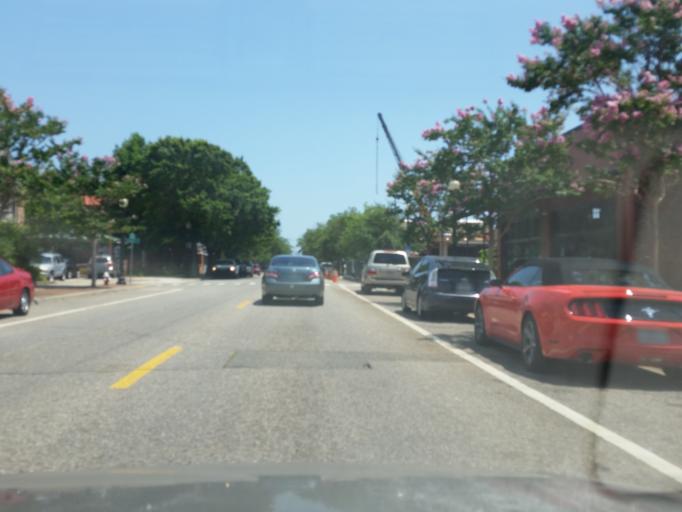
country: US
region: Florida
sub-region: Escambia County
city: Pensacola
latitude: 30.4063
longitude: -87.2139
